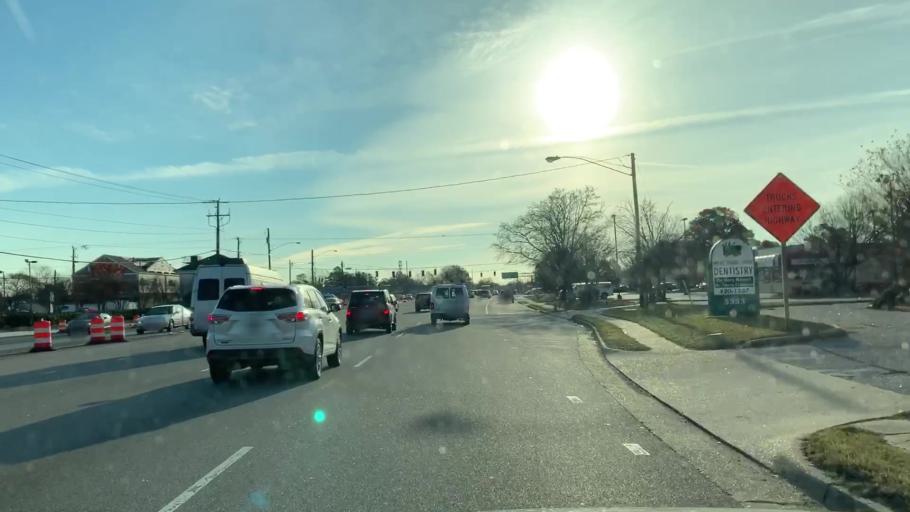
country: US
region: Virginia
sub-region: City of Chesapeake
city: Chesapeake
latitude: 36.7983
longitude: -76.1767
